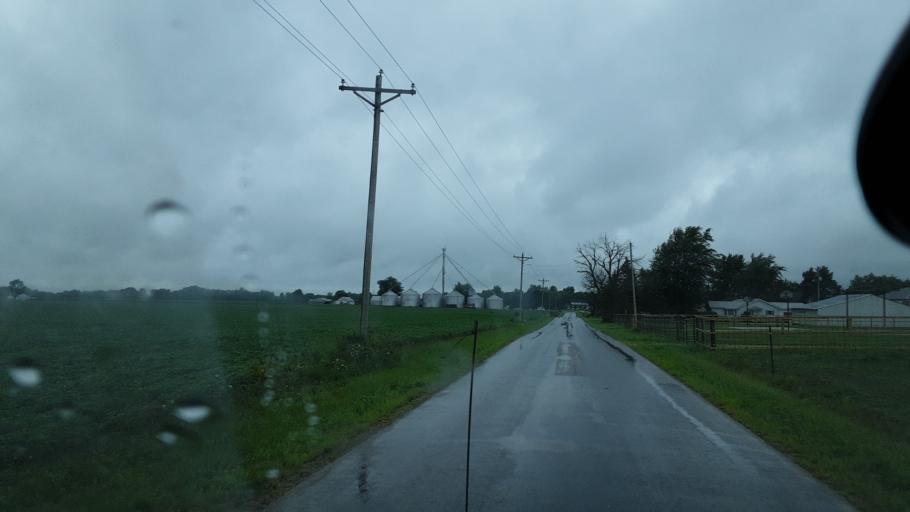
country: US
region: Indiana
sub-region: Adams County
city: Decatur
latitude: 40.7708
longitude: -84.8607
